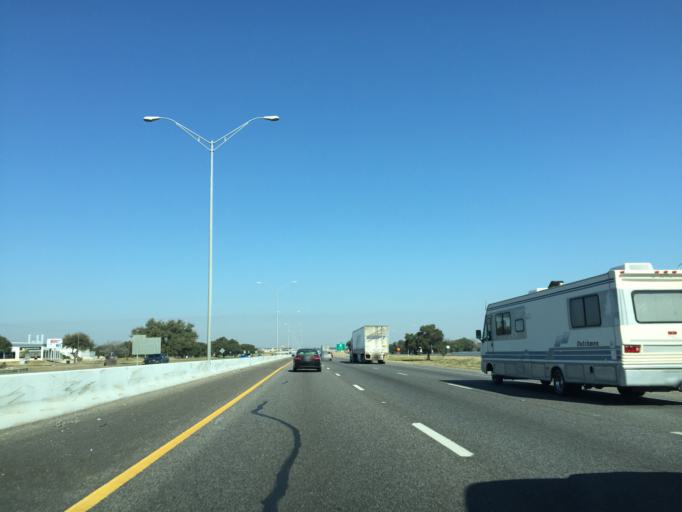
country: US
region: Texas
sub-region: Williamson County
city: Georgetown
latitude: 30.6126
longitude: -97.6872
